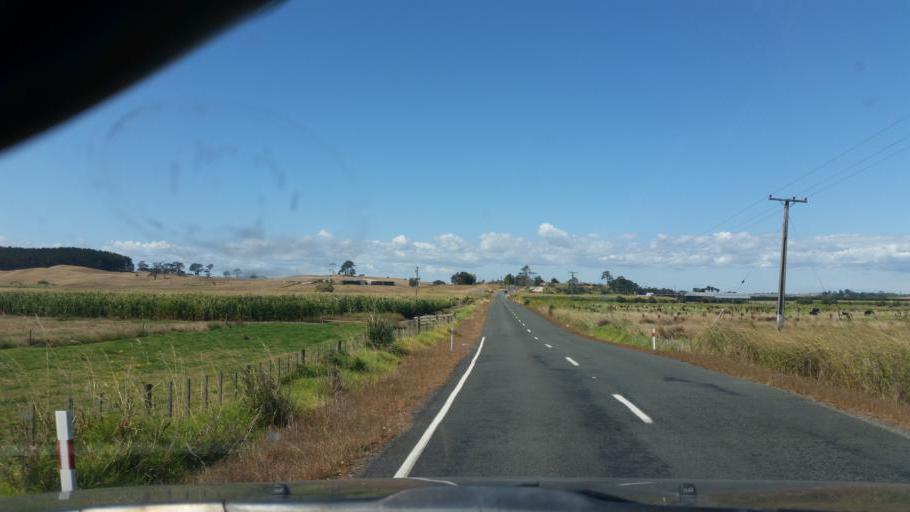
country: NZ
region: Northland
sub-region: Kaipara District
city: Dargaville
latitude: -35.9488
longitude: 173.8048
